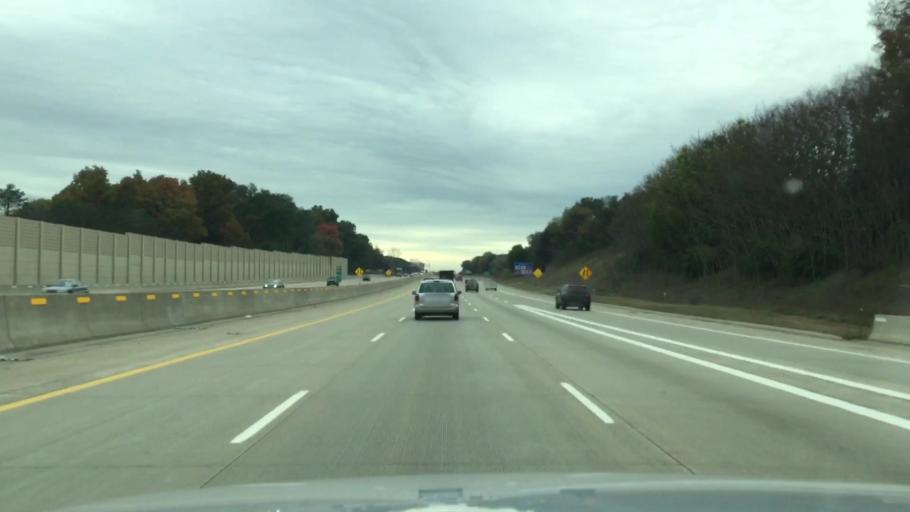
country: US
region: Michigan
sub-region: Kalamazoo County
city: Westwood
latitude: 42.2381
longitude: -85.6447
